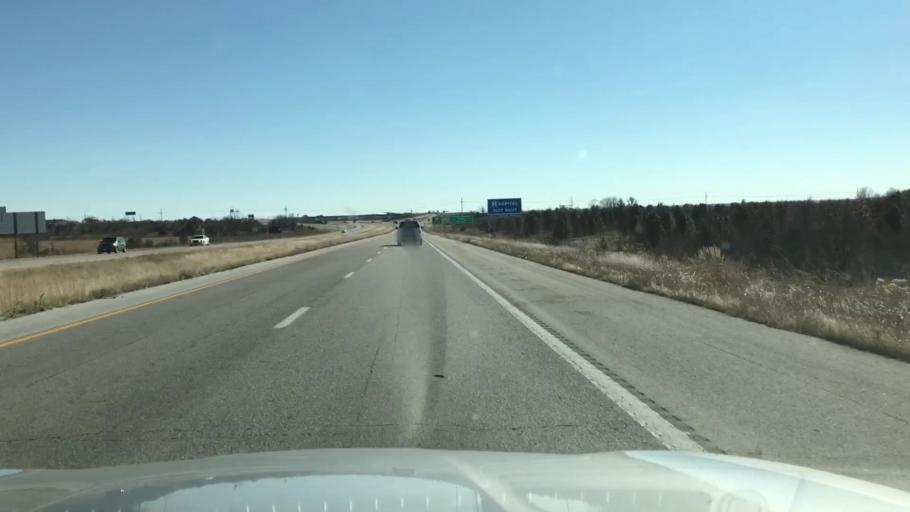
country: US
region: Missouri
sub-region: Jasper County
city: Carthage
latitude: 37.1472
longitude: -94.3276
